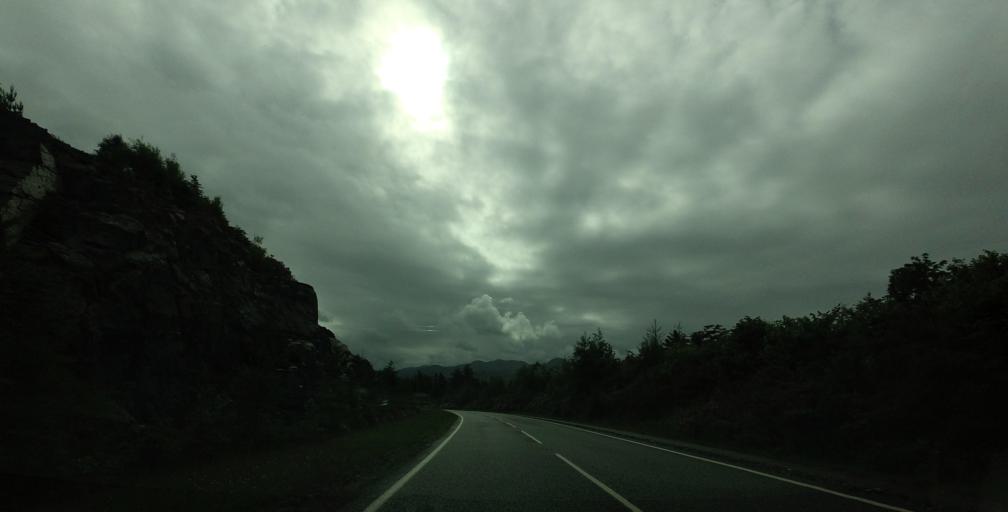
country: GB
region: Scotland
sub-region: Argyll and Bute
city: Isle Of Mull
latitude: 56.8993
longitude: -5.8003
